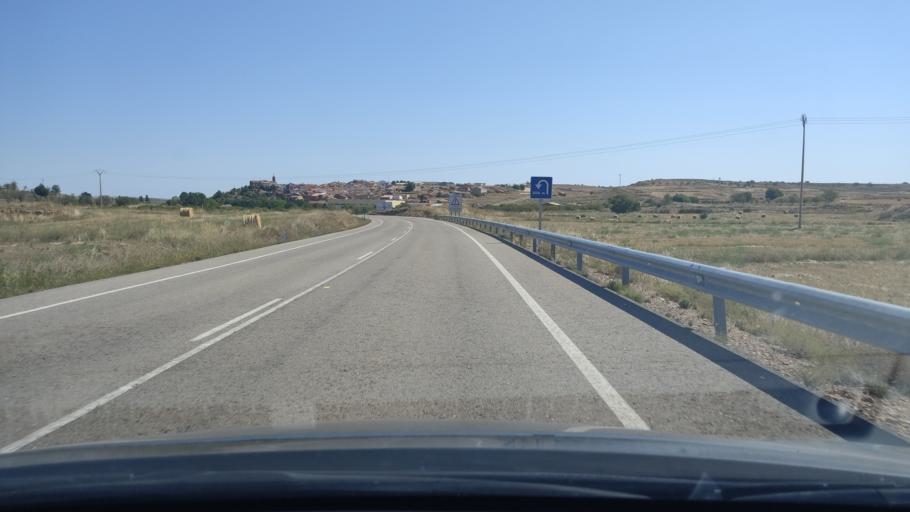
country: ES
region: Aragon
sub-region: Provincia de Teruel
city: Cortes de Aragon
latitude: 40.9704
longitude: -0.8444
